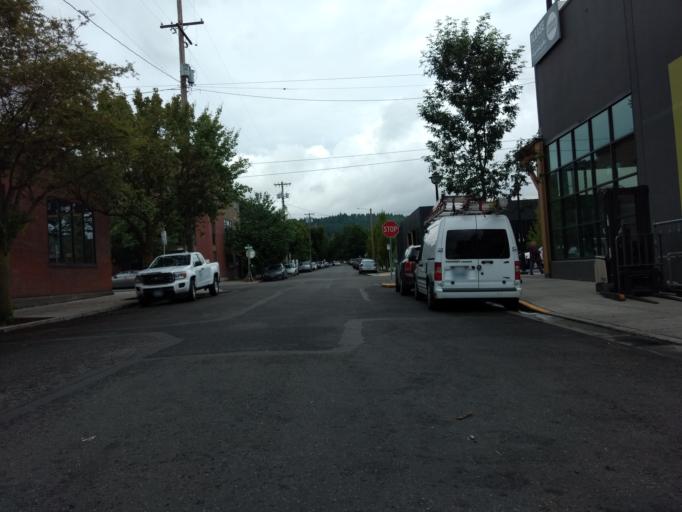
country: US
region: Oregon
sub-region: Multnomah County
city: Portland
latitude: 45.5334
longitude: -122.6963
